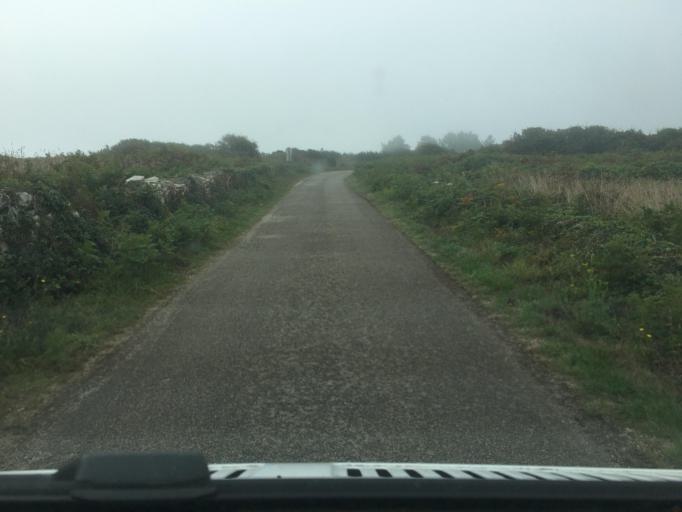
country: FR
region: Brittany
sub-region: Departement du Finistere
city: Plogoff
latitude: 48.0348
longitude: -4.6954
